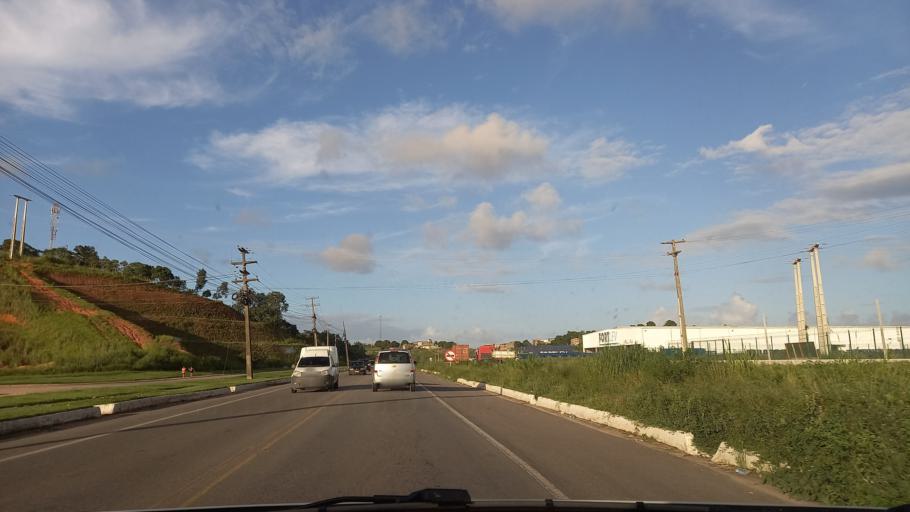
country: BR
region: Pernambuco
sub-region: Cabo De Santo Agostinho
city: Cabo
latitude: -8.2456
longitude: -34.9945
